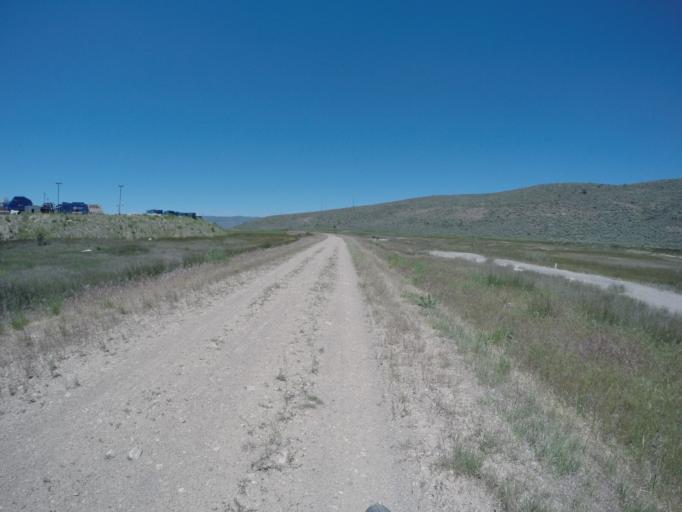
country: US
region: Utah
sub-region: Summit County
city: Park City
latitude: 40.6872
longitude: -111.4572
